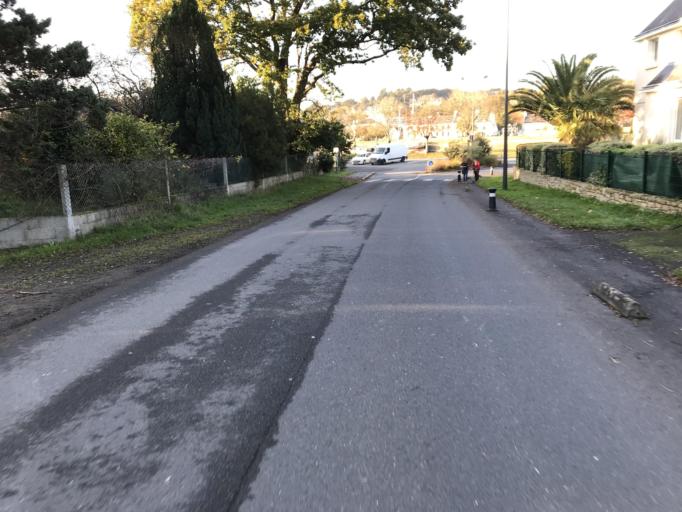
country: FR
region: Brittany
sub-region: Departement du Finistere
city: Le Faou
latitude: 48.2948
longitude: -4.1826
